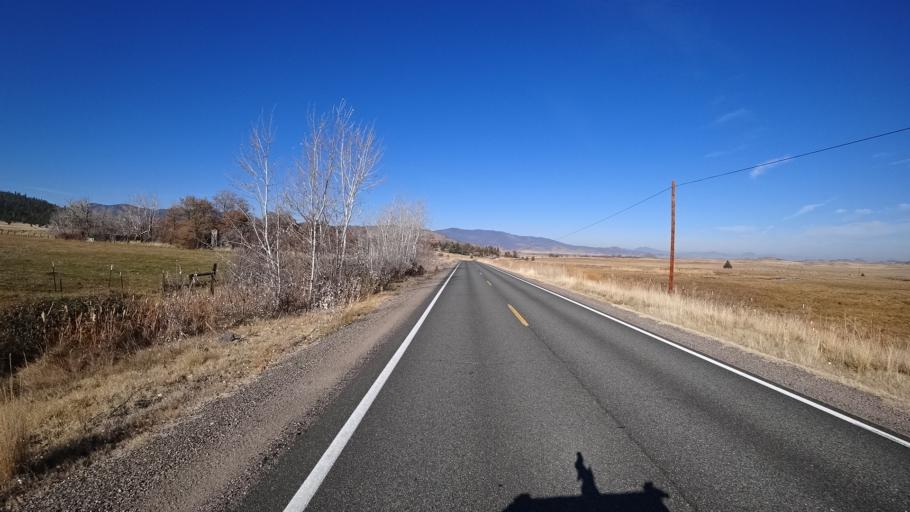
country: US
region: California
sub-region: Siskiyou County
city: Weed
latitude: 41.4902
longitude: -122.5061
